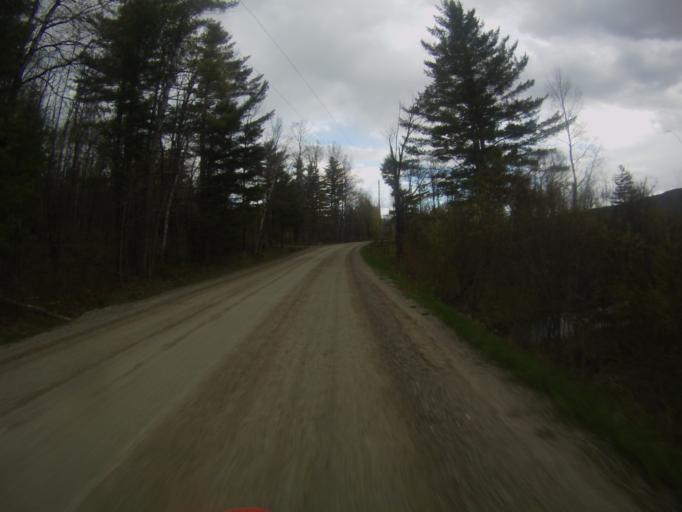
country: US
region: Vermont
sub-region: Addison County
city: Bristol
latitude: 44.0405
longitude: -73.0149
